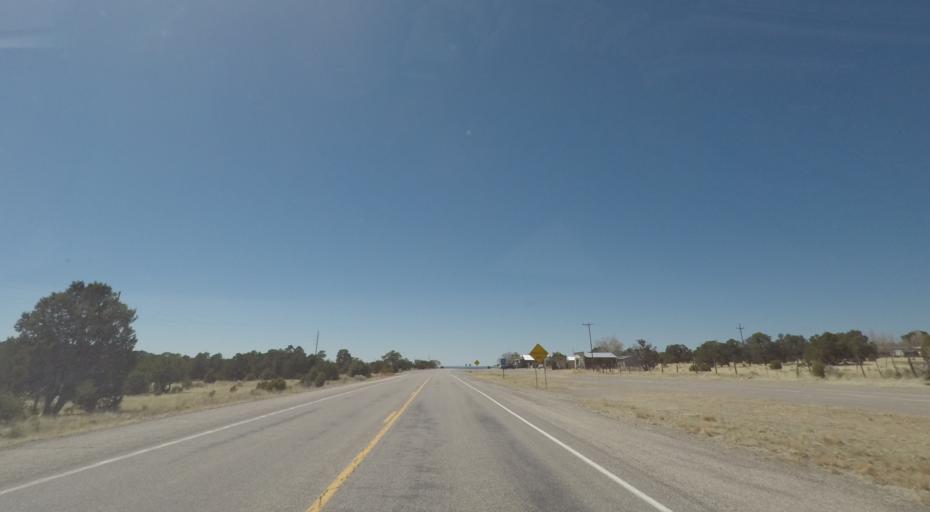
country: US
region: New Mexico
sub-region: Socorro County
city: Alamo
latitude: 34.2982
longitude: -108.1284
